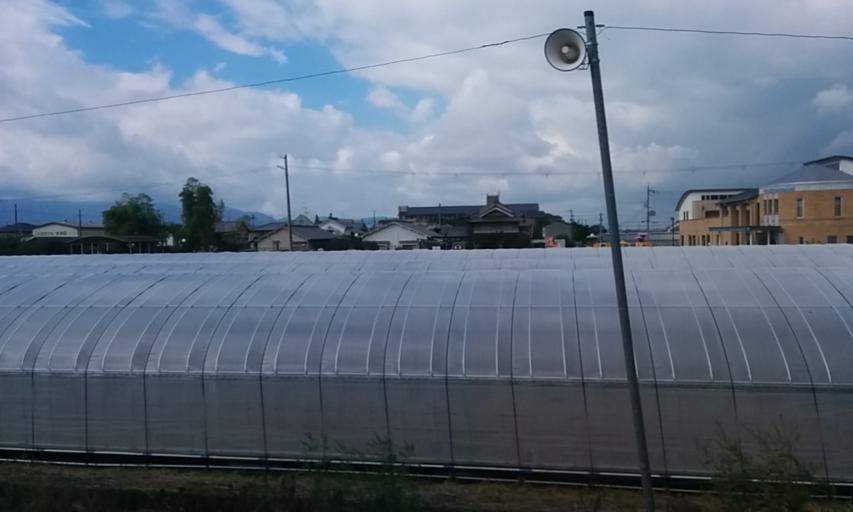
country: JP
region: Nara
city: Tawaramoto
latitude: 34.5394
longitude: 135.7940
